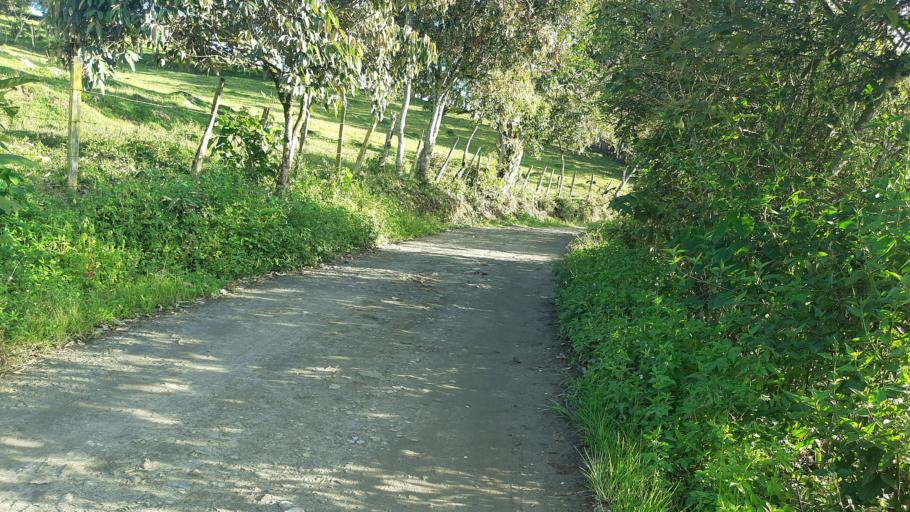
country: CO
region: Boyaca
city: Garagoa
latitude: 5.0891
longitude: -73.3619
